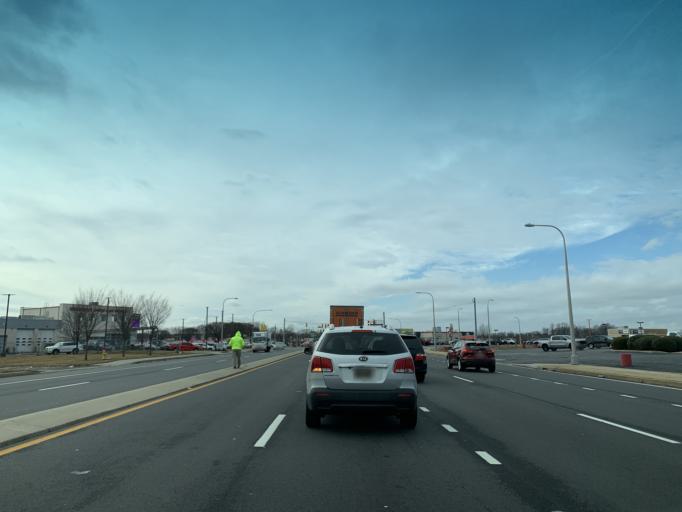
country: US
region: Delaware
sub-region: New Castle County
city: Wilmington Manor
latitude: 39.6654
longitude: -75.6025
